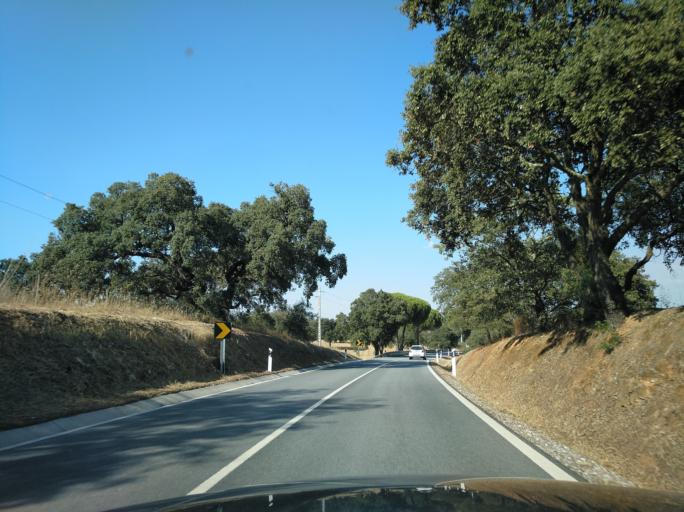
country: ES
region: Andalusia
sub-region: Provincia de Huelva
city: Rosal de la Frontera
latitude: 38.0051
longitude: -7.2839
